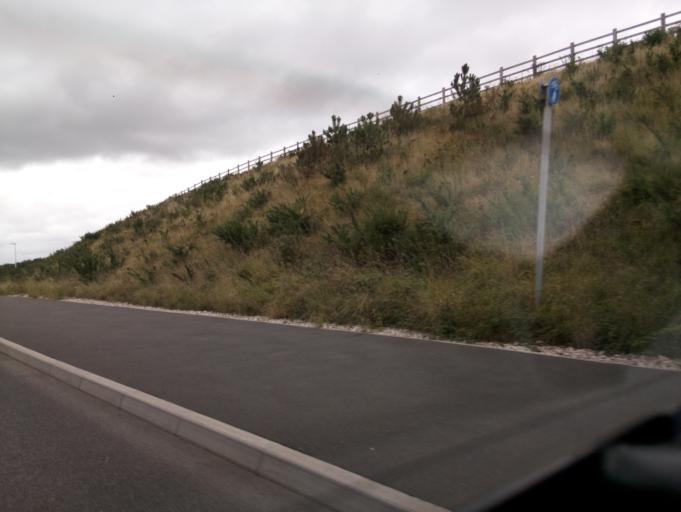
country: GB
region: England
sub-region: Devon
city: Marldon
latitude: 50.4496
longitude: -3.5922
